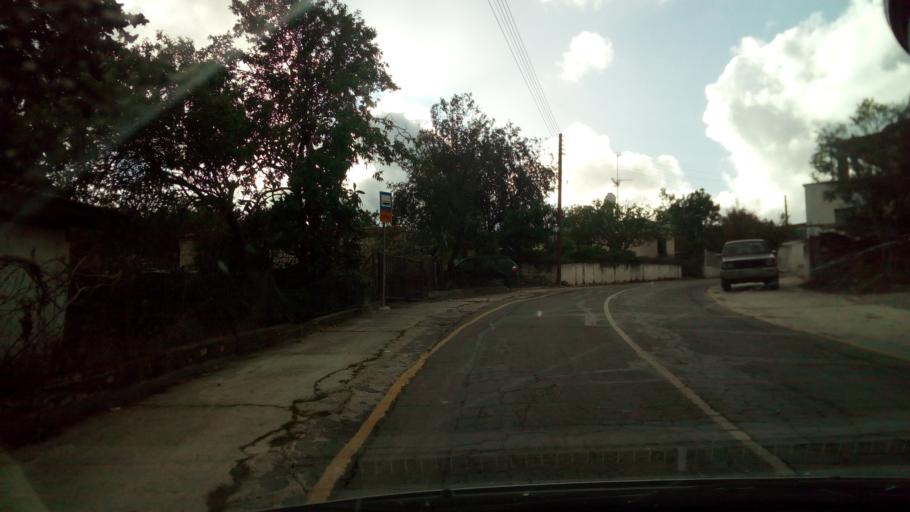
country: CY
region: Pafos
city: Mesogi
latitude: 34.8576
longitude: 32.5115
